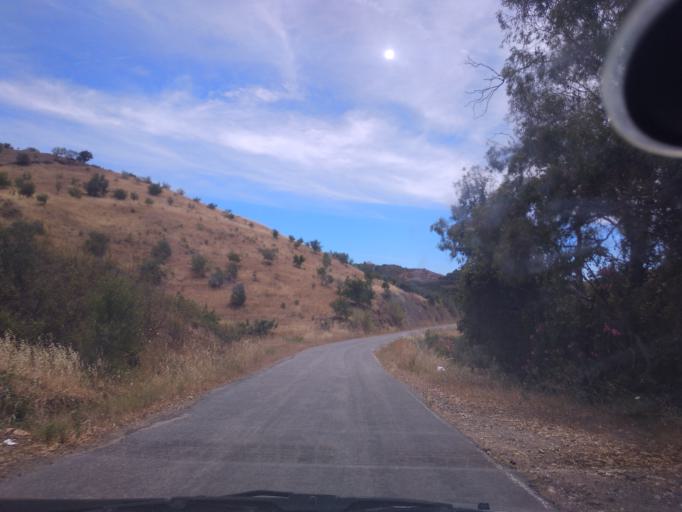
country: PT
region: Faro
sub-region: Olhao
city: Moncarapacho
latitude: 37.1657
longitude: -7.8013
